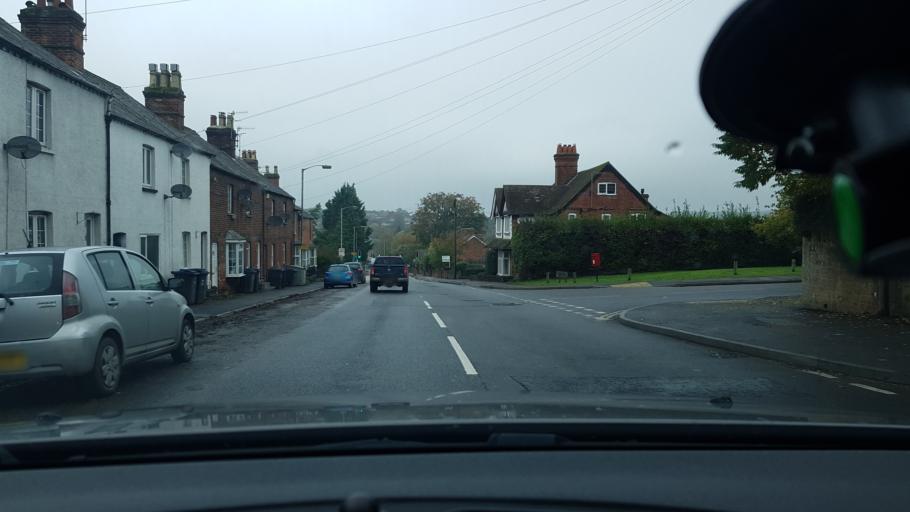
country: GB
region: England
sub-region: Wiltshire
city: Marlborough
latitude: 51.4170
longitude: -1.7235
